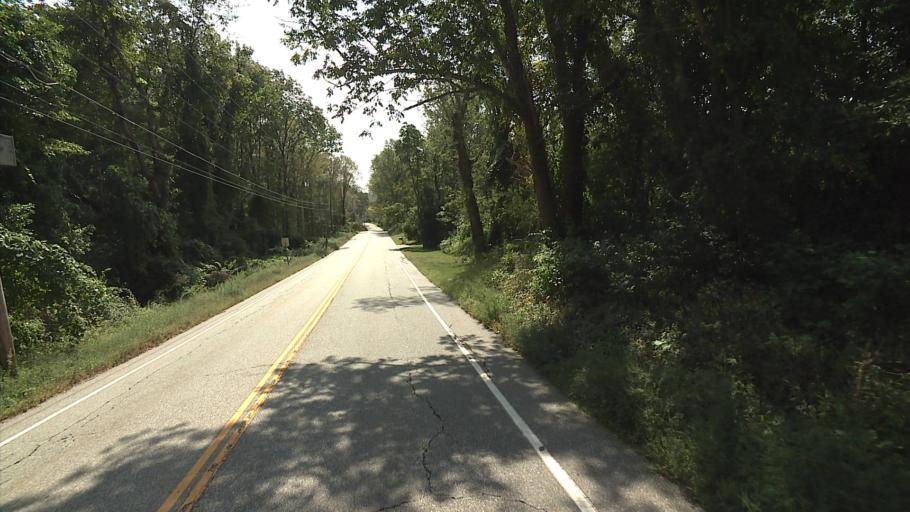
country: US
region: Connecticut
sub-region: Windham County
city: East Brooklyn
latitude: 41.8121
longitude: -71.9558
